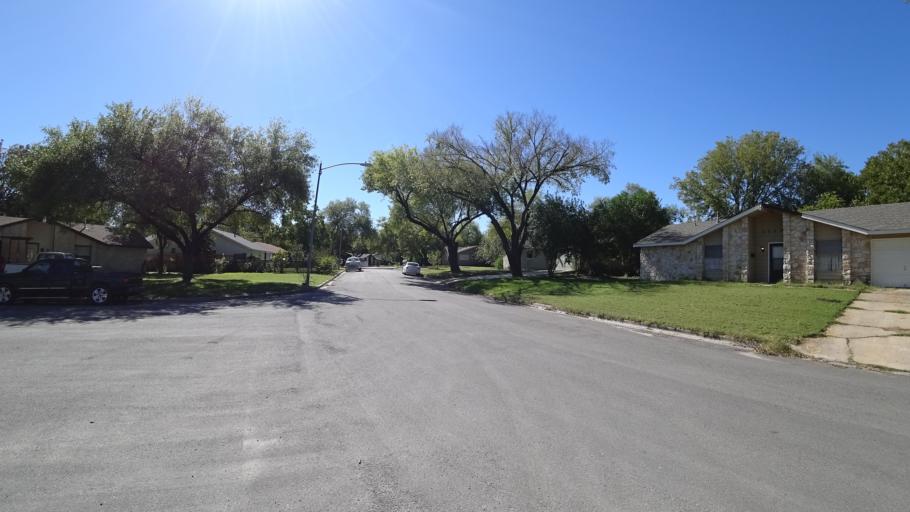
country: US
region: Texas
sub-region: Travis County
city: Austin
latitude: 30.2877
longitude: -97.6619
